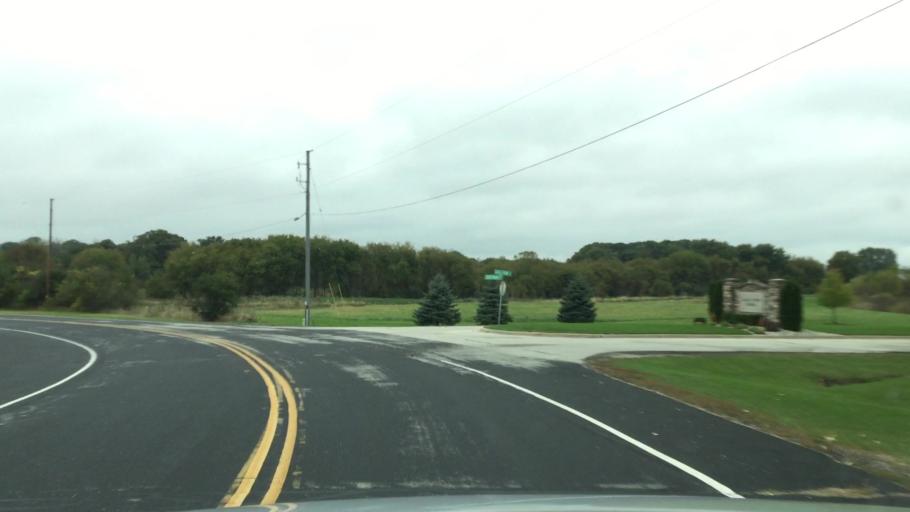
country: US
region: Wisconsin
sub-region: Racine County
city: Waterford
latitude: 42.7629
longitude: -88.1654
